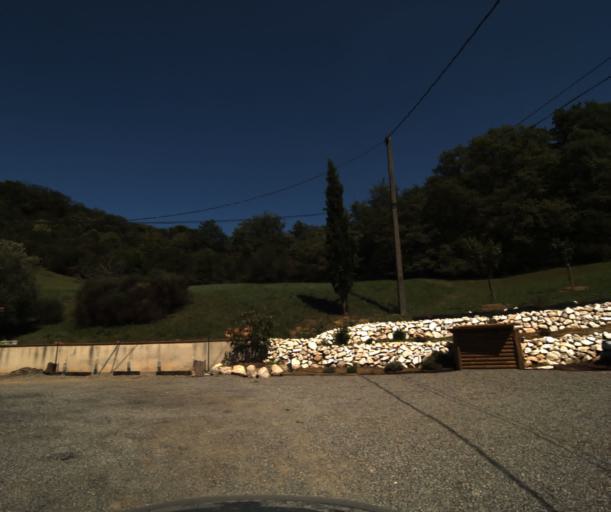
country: FR
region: Midi-Pyrenees
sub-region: Departement de la Haute-Garonne
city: Le Fauga
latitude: 43.4129
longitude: 1.3186
